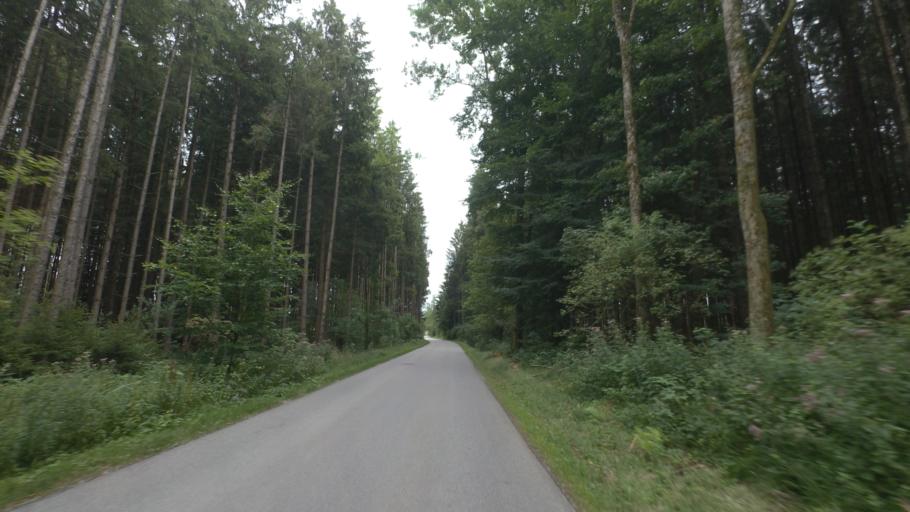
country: DE
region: Bavaria
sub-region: Upper Bavaria
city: Pittenhart
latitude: 47.9858
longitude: 12.3780
